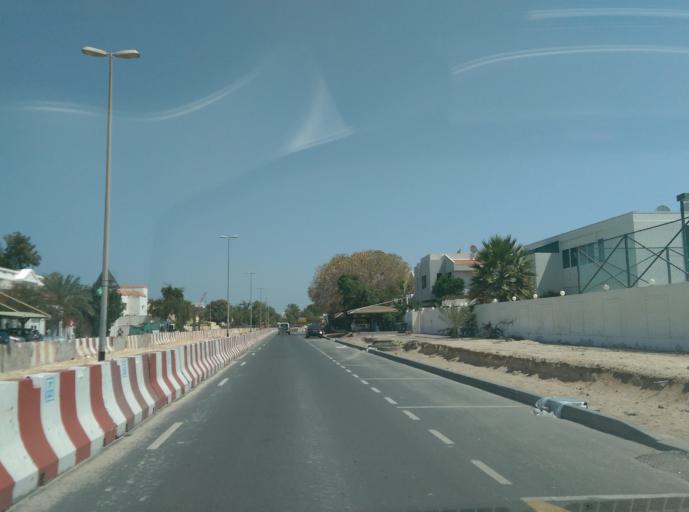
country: AE
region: Dubai
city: Dubai
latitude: 25.1894
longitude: 55.2353
